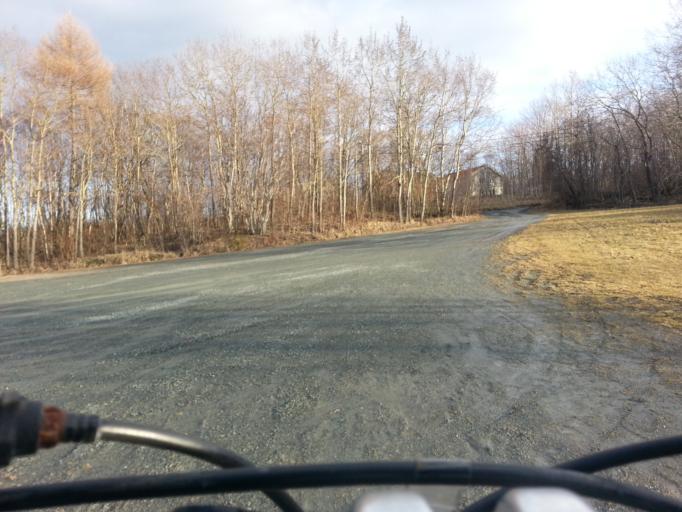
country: NO
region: Sor-Trondelag
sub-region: Trondheim
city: Trondheim
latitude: 63.4557
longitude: 10.4509
